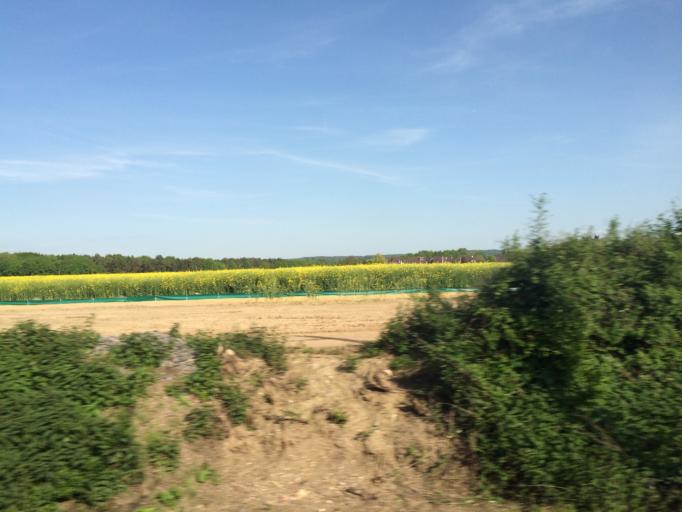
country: DE
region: North Rhine-Westphalia
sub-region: Regierungsbezirk Koln
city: Troisdorf
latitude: 50.7629
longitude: 7.1392
